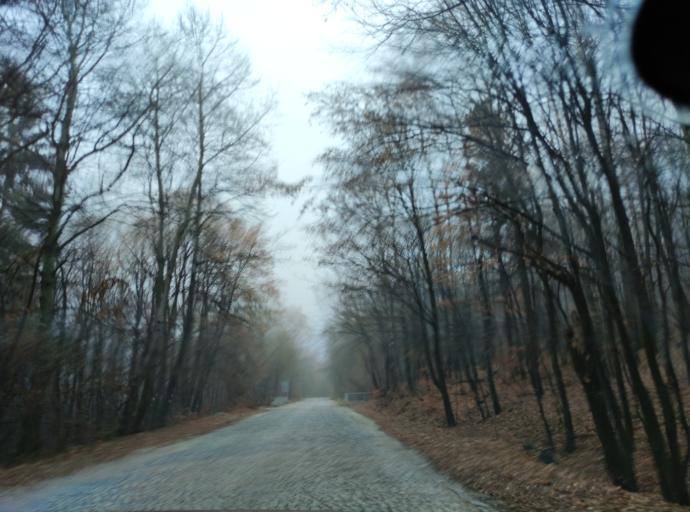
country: BG
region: Sofia-Capital
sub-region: Stolichna Obshtina
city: Sofia
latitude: 42.6223
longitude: 23.3023
